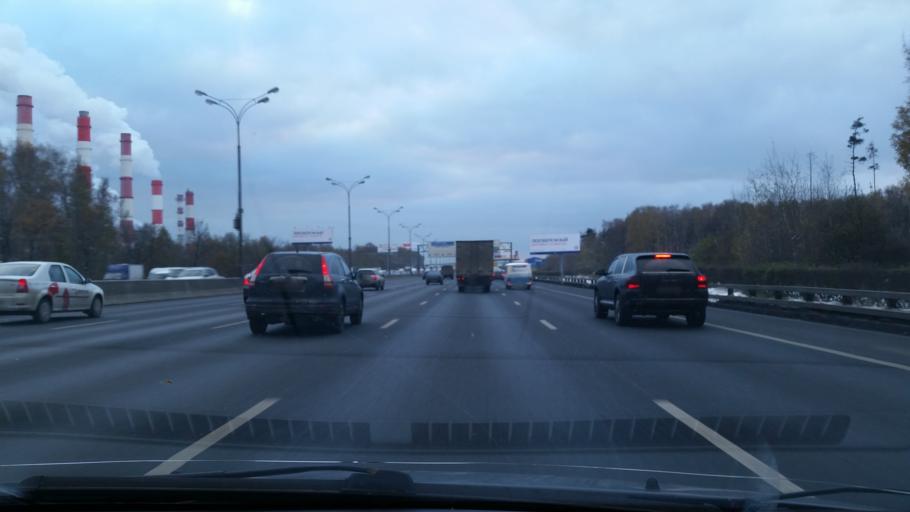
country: RU
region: Moscow
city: Businovo
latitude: 55.8999
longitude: 37.5139
